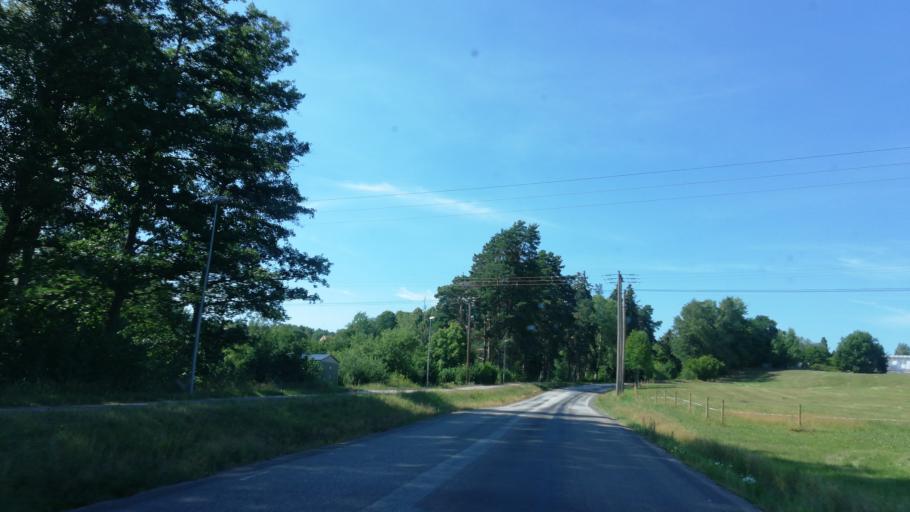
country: SE
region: OEstergoetland
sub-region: Finspangs Kommun
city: Finspang
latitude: 58.7296
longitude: 15.8296
